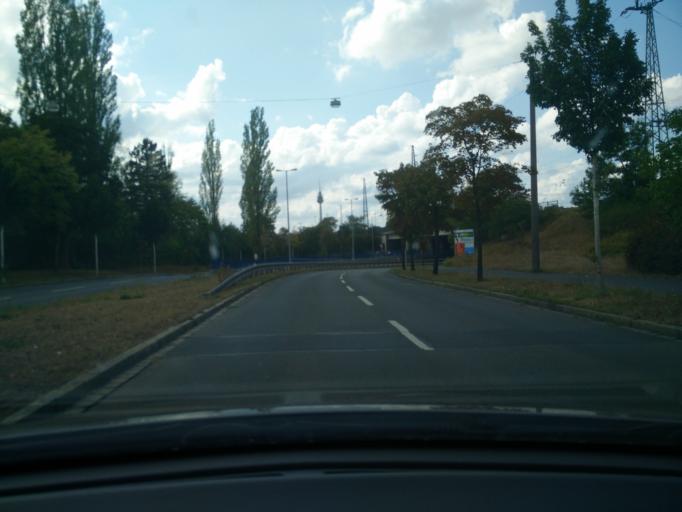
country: DE
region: Bavaria
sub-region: Regierungsbezirk Mittelfranken
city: Nuernberg
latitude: 49.4199
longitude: 11.0693
